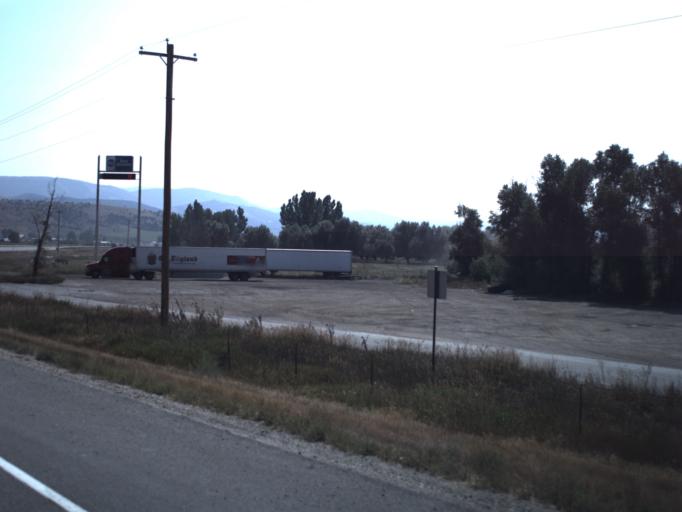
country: US
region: Utah
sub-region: Summit County
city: Coalville
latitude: 40.9110
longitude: -111.4029
